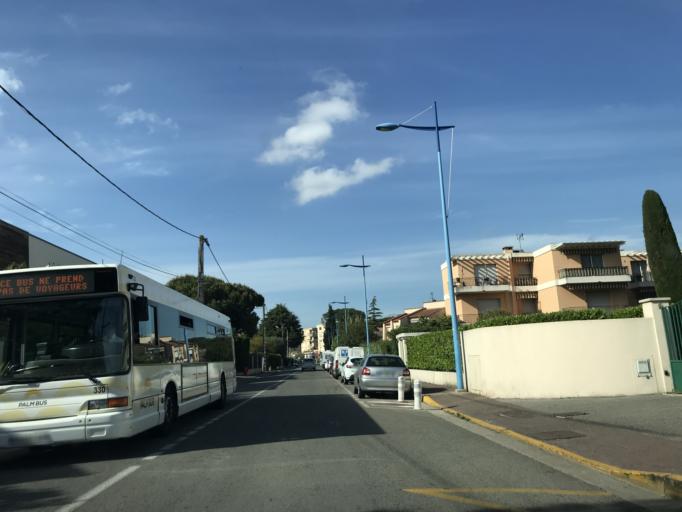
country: FR
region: Provence-Alpes-Cote d'Azur
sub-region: Departement des Alpes-Maritimes
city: Mandelieu-la-Napoule
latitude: 43.5395
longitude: 6.9419
